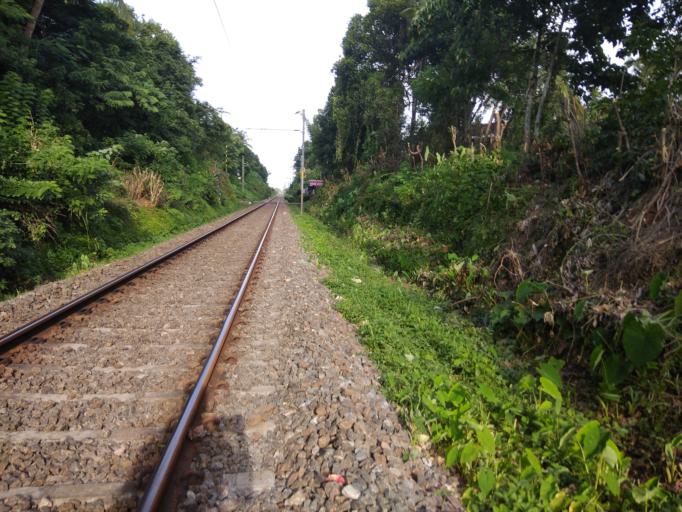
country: IN
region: Kerala
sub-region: Thrissur District
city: Avanoor
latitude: 10.5607
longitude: 76.1759
